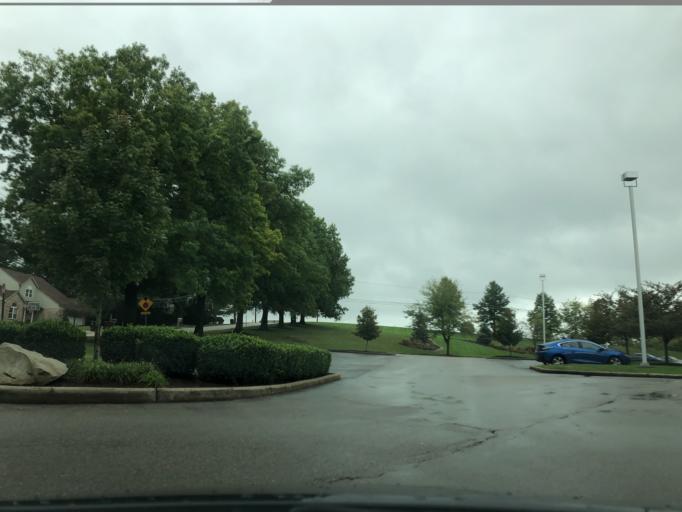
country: US
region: Ohio
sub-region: Hamilton County
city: Finneytown
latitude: 39.2088
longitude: -84.5030
